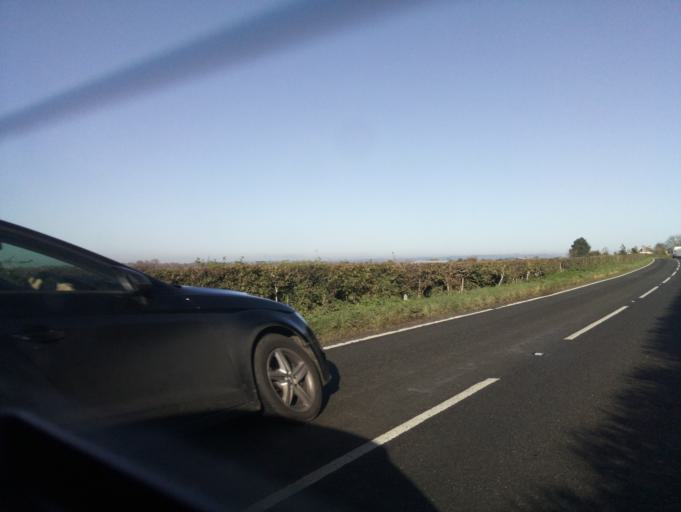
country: GB
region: England
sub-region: Somerset
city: Langport
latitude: 51.0696
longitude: -2.8558
